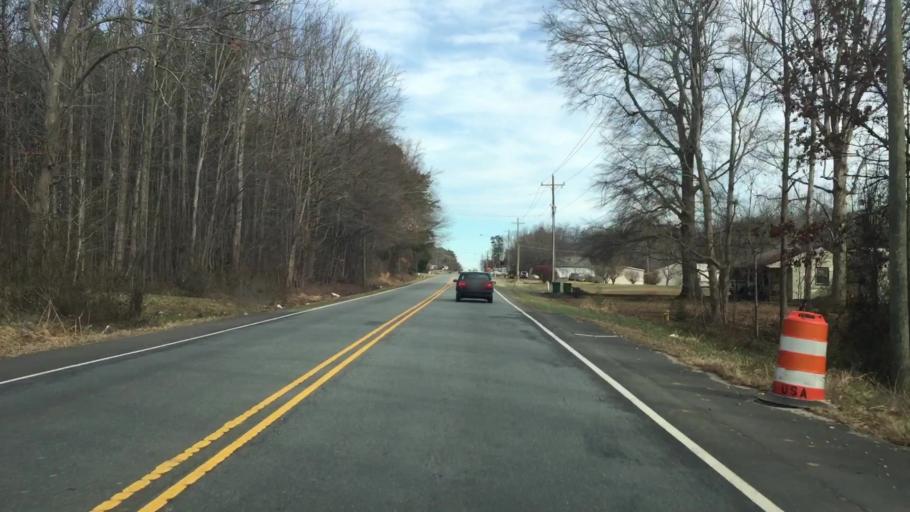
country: US
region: North Carolina
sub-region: Forsyth County
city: Walkertown
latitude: 36.1510
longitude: -80.1514
